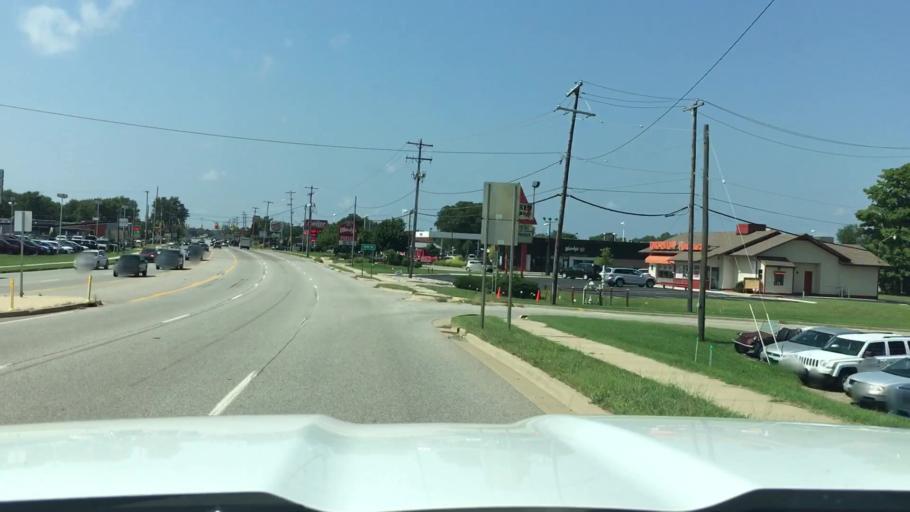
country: US
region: Michigan
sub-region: Allegan County
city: Plainwell
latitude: 42.4499
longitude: -85.6584
